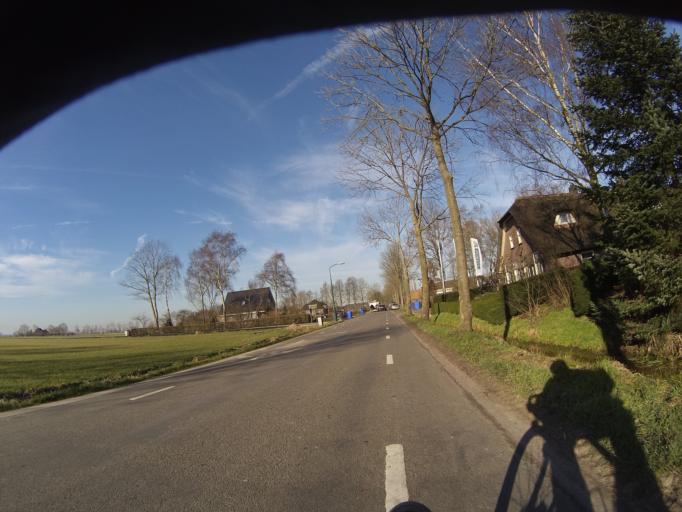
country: NL
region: Utrecht
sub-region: Gemeente Amersfoort
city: Hoogland
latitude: 52.2090
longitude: 5.3886
